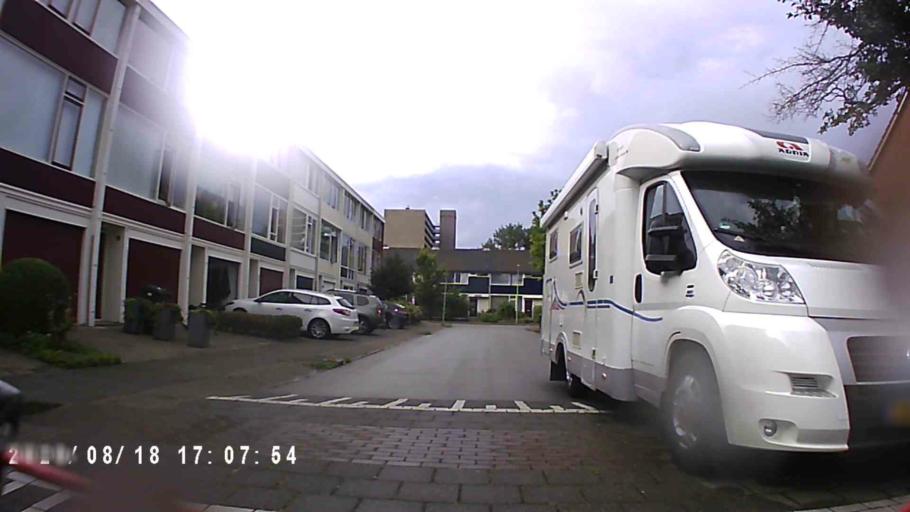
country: NL
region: Groningen
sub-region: Gemeente Groningen
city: Korrewegwijk
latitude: 53.2304
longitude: 6.5250
